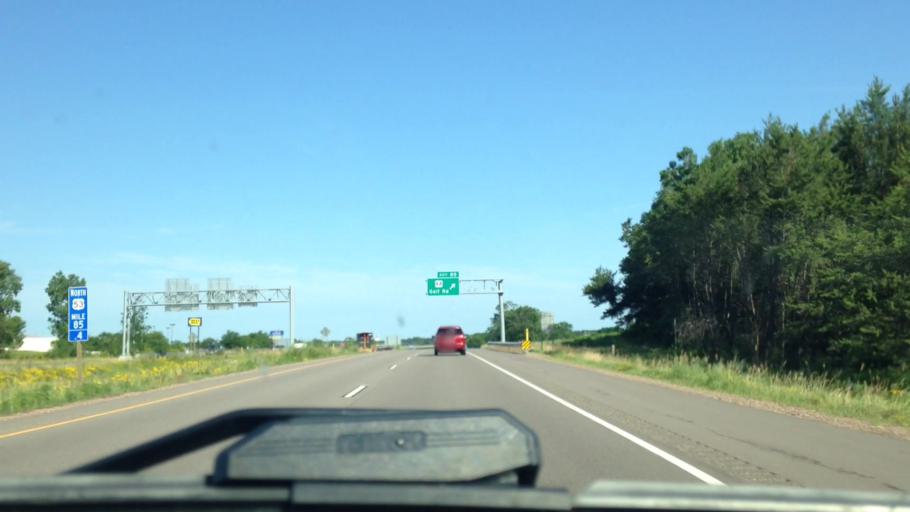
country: US
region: Wisconsin
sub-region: Eau Claire County
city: Altoona
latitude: 44.7728
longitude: -91.4284
